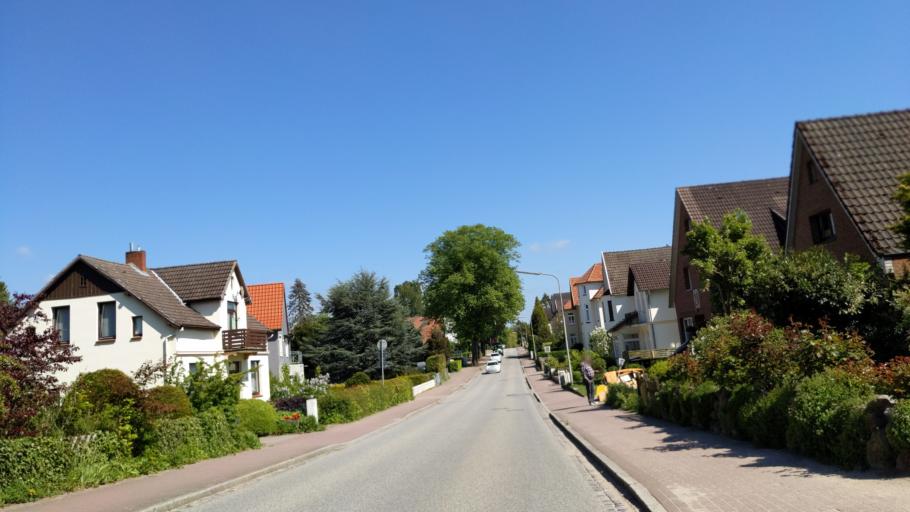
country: DE
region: Schleswig-Holstein
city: Malente
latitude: 54.1658
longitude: 10.5595
